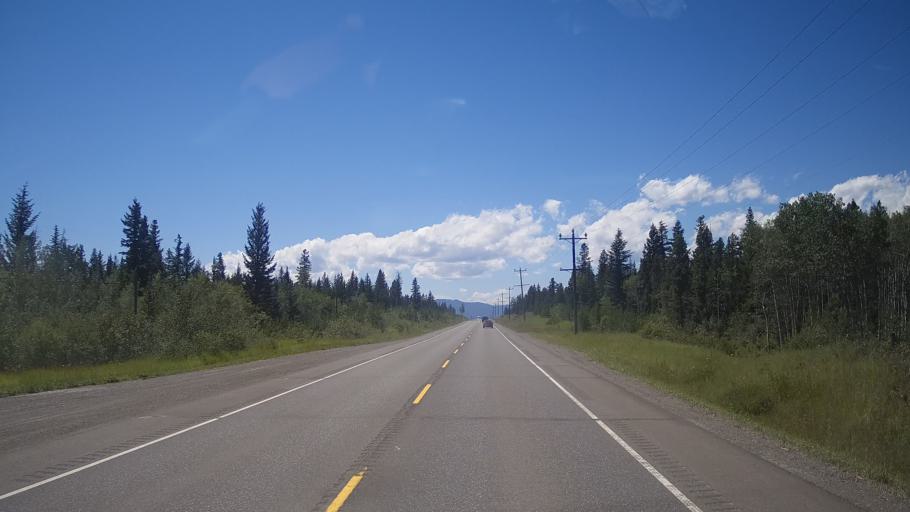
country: CA
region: British Columbia
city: Cache Creek
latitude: 51.2164
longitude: -121.5226
